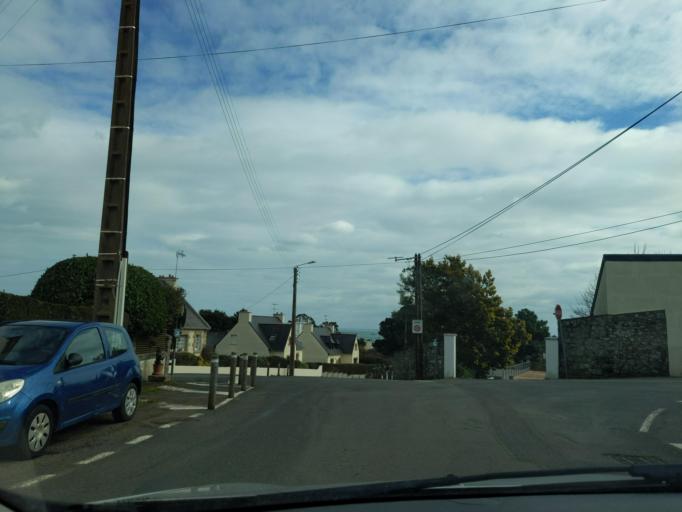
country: FR
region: Brittany
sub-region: Departement des Cotes-d'Armor
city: Saint-Quay-Portrieux
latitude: 48.6627
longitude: -2.8467
